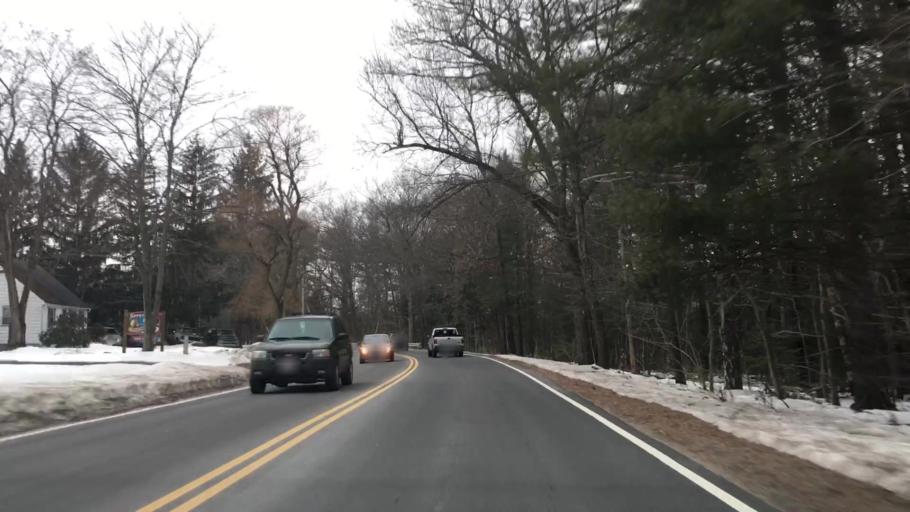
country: US
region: Massachusetts
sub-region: Hampden County
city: Westfield
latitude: 42.1039
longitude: -72.6924
